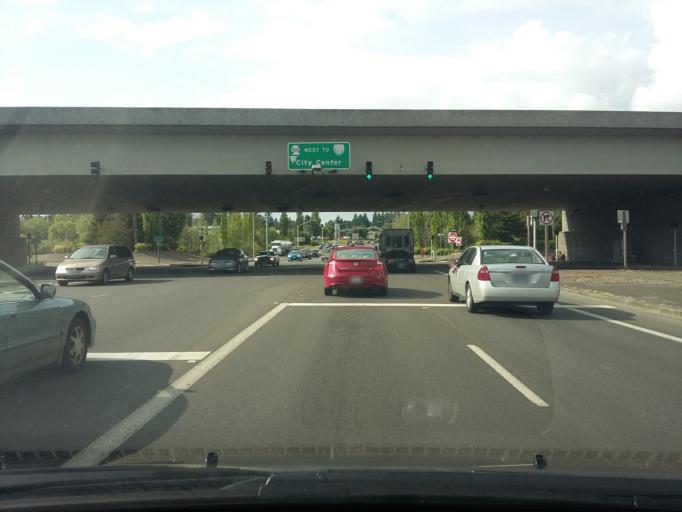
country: US
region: Washington
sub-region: Clark County
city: Walnut Grove
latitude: 45.6482
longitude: -122.6013
